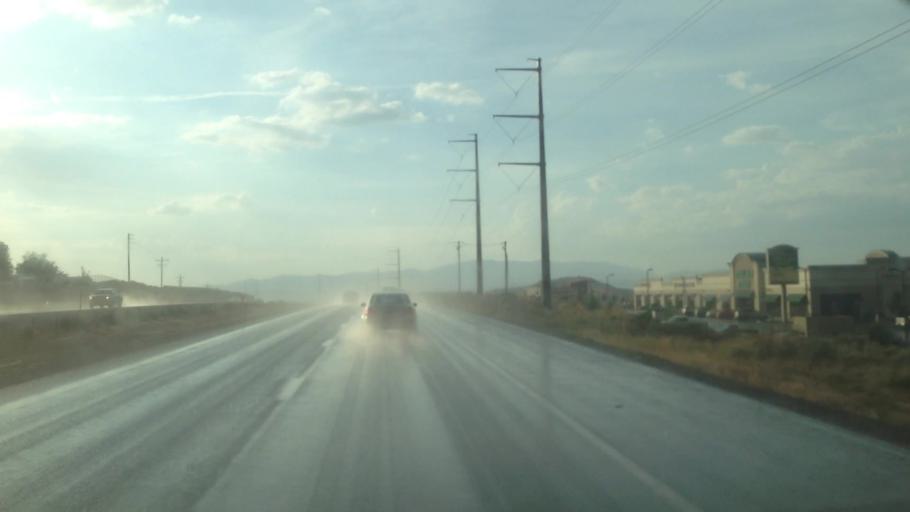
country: US
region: Nevada
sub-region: Washoe County
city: Golden Valley
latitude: 39.6038
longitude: -119.8410
